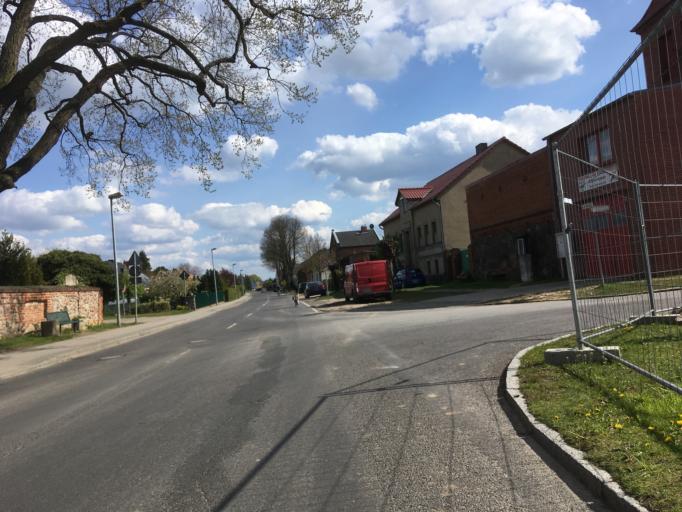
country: DE
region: Brandenburg
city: Altlandsberg
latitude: 52.5963
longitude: 13.6924
